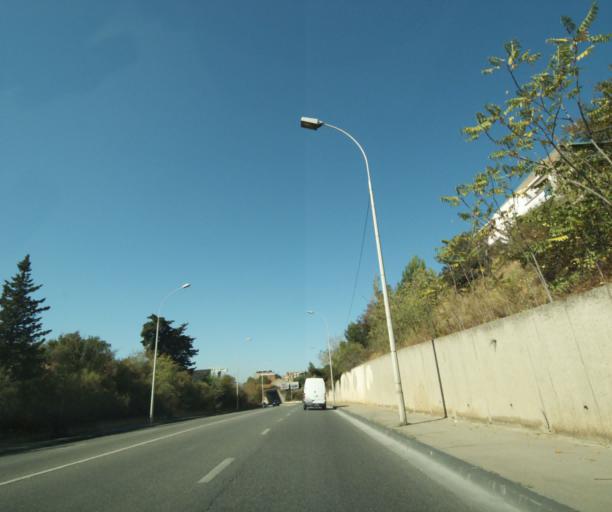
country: FR
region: Provence-Alpes-Cote d'Azur
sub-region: Departement des Bouches-du-Rhone
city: Marseille 14
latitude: 43.3397
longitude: 5.3905
